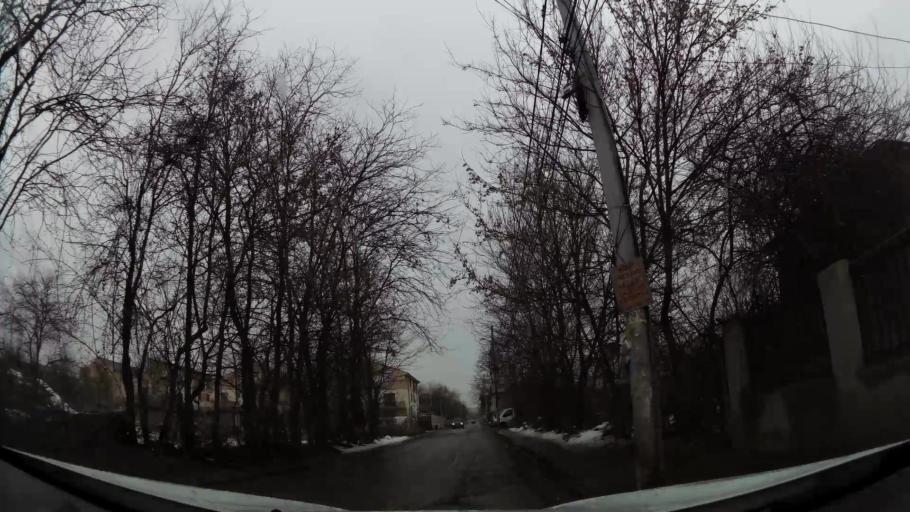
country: RO
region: Ilfov
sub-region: Comuna Chiajna
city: Rosu
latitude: 44.4052
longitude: 26.0153
